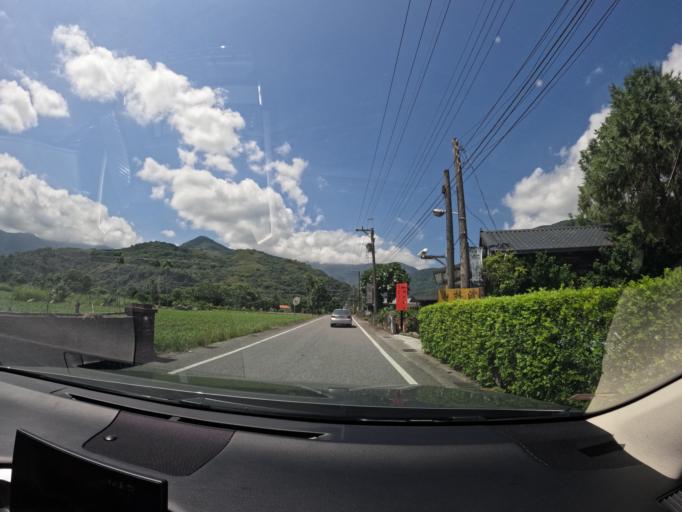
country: TW
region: Taiwan
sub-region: Hualien
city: Hualian
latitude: 23.7137
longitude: 121.4180
